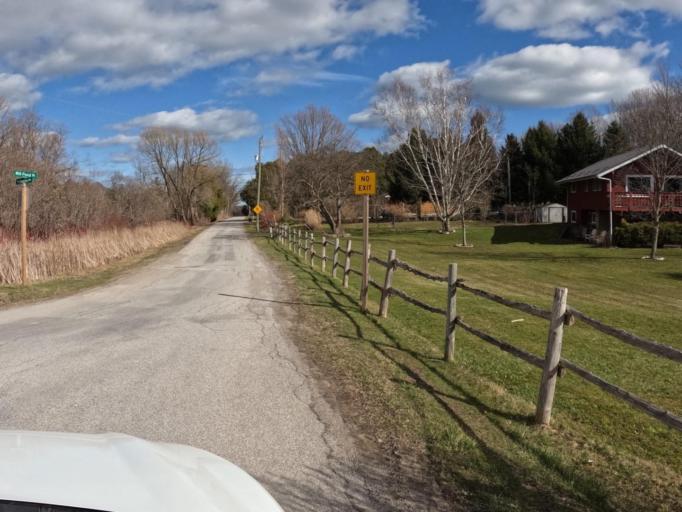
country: CA
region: Ontario
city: Norfolk County
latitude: 42.7673
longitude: -80.3102
